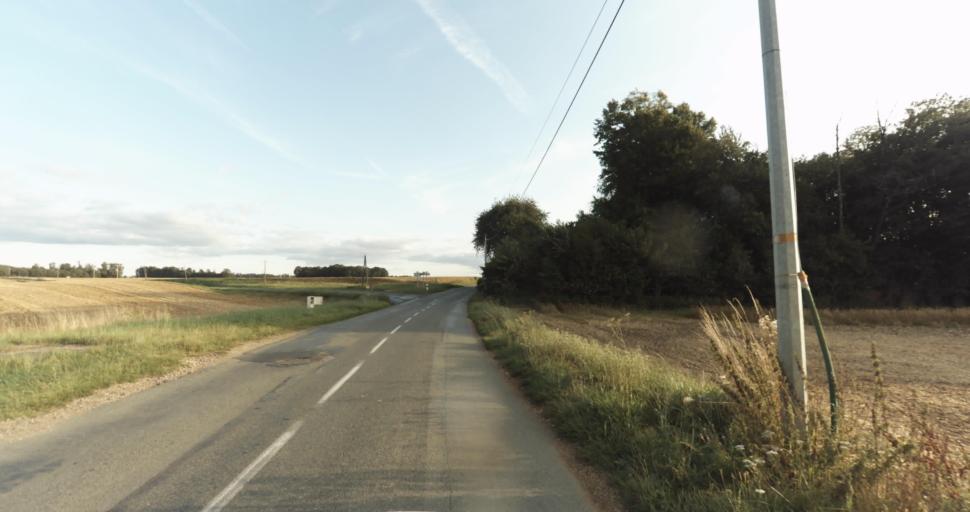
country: FR
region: Haute-Normandie
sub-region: Departement de l'Eure
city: Marcilly-sur-Eure
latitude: 48.8807
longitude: 1.2633
